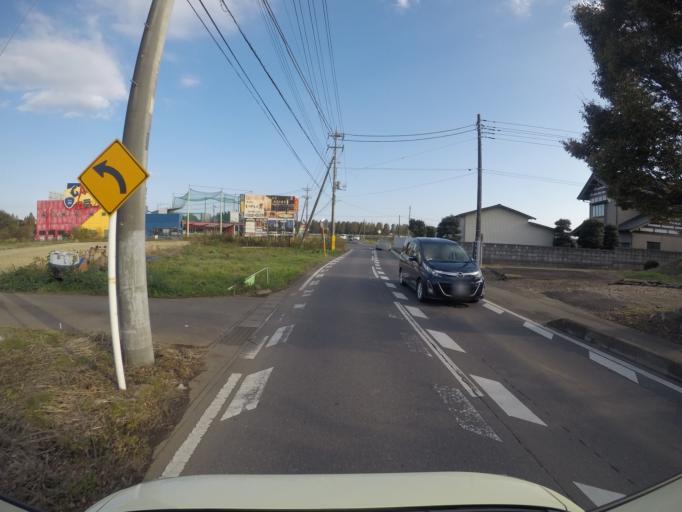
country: JP
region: Ibaraki
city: Naka
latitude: 36.0588
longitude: 140.0994
